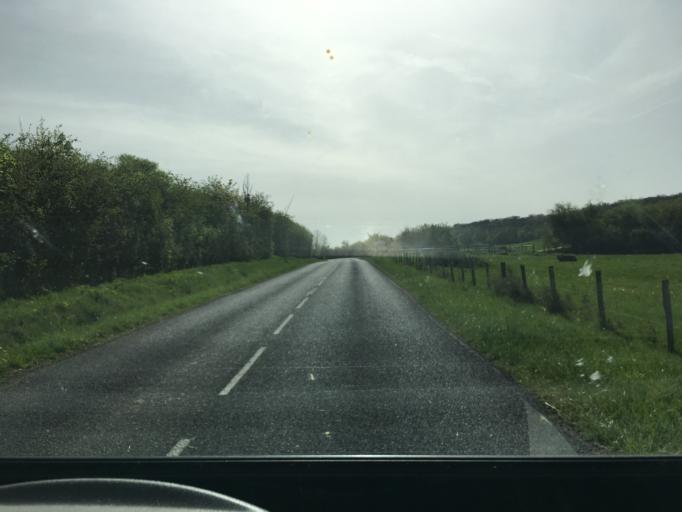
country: FR
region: Lorraine
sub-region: Departement de Meurthe-et-Moselle
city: Dommartin-les-Toul
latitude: 48.6701
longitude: 5.9369
